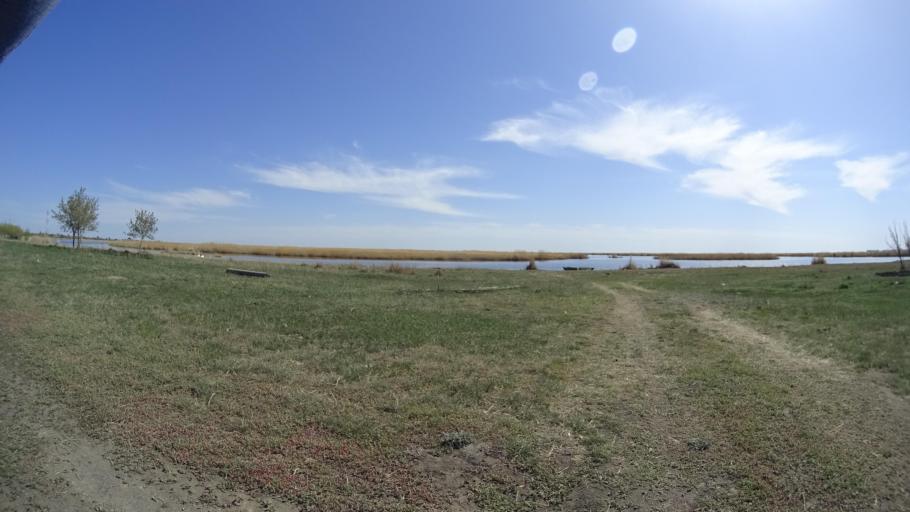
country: RU
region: Chelyabinsk
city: Chesma
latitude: 53.7983
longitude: 61.0176
